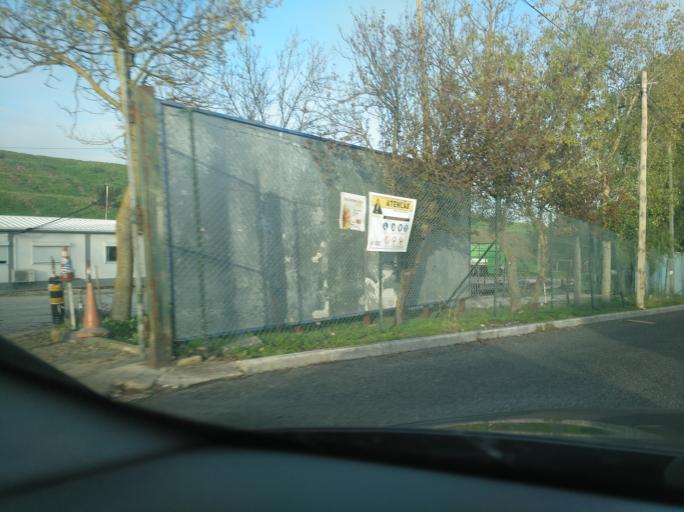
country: PT
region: Lisbon
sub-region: Odivelas
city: Odivelas
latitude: 38.7755
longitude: -9.1803
